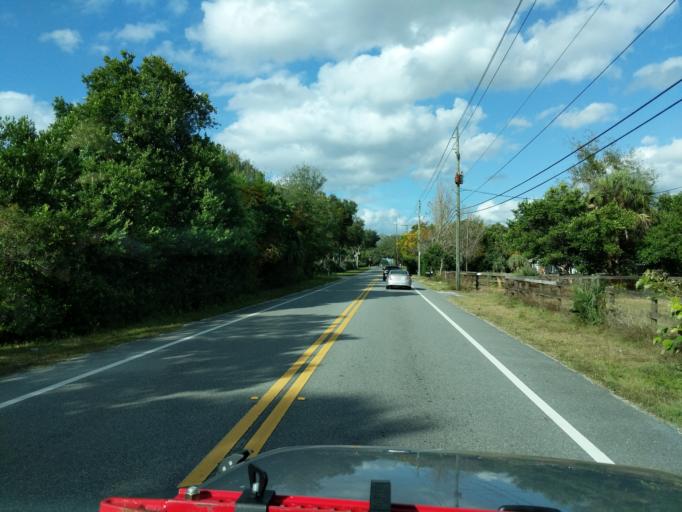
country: US
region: Florida
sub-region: Seminole County
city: Geneva
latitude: 28.7245
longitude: -81.1150
